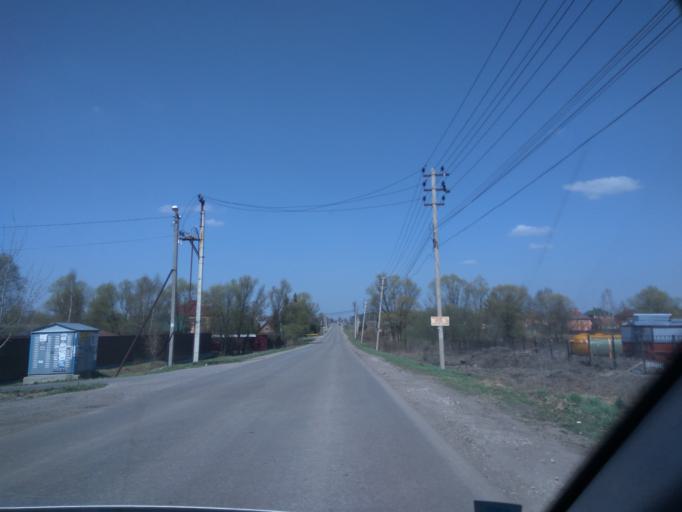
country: RU
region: Moskovskaya
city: Ramenskoye
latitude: 55.5682
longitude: 38.2972
